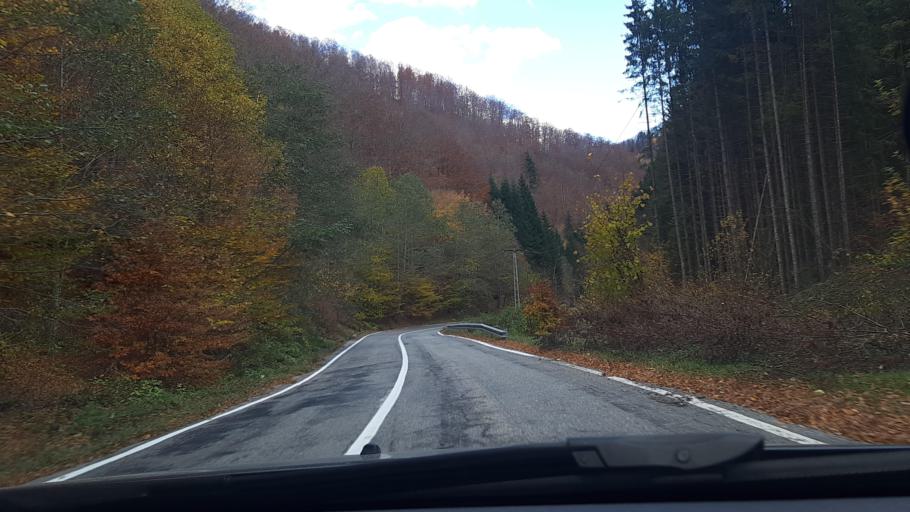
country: RO
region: Valcea
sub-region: Comuna Voineasa
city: Voineasa
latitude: 45.4294
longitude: 23.9073
